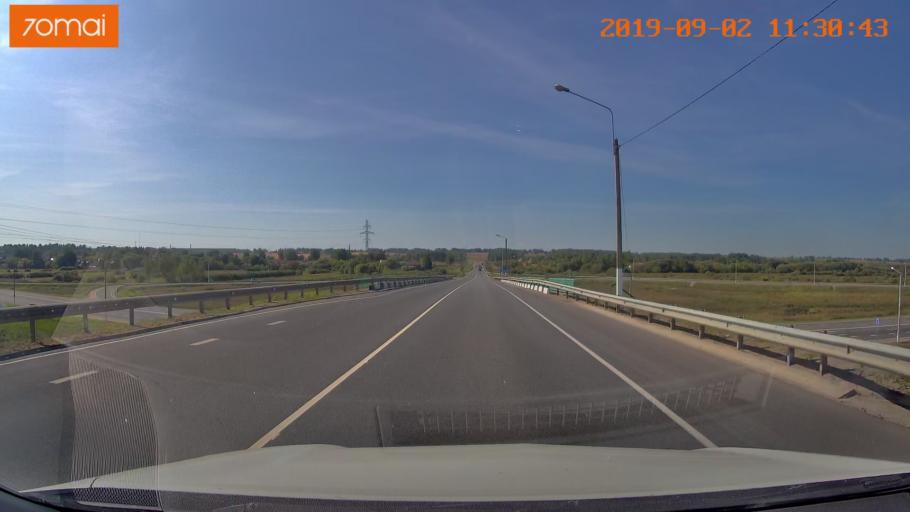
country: RU
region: Smolensk
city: Oster
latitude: 53.9814
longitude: 32.8282
